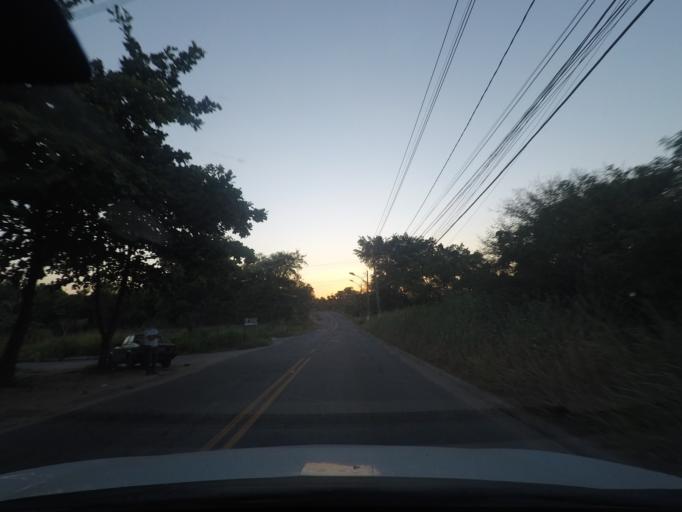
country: BR
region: Rio de Janeiro
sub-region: Sao Goncalo
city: Sao Goncalo
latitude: -22.9483
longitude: -42.9686
